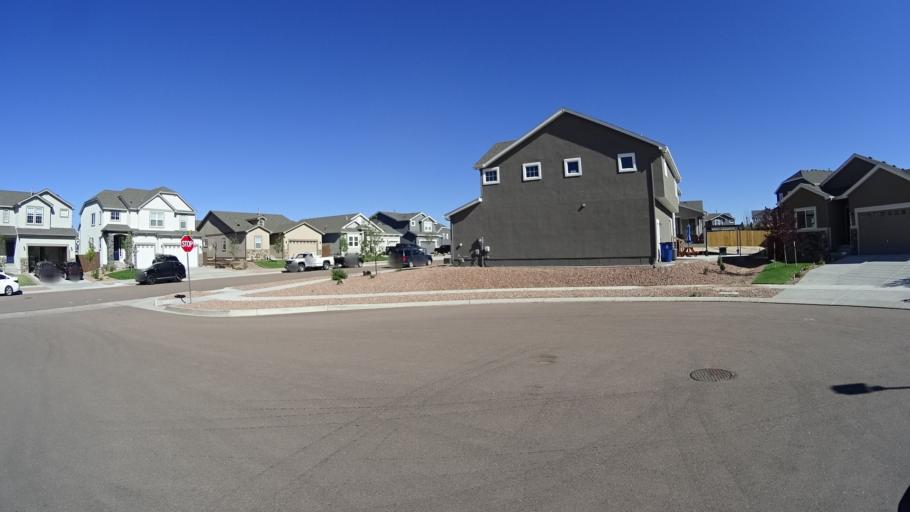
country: US
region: Colorado
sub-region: El Paso County
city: Black Forest
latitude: 38.9506
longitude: -104.6739
